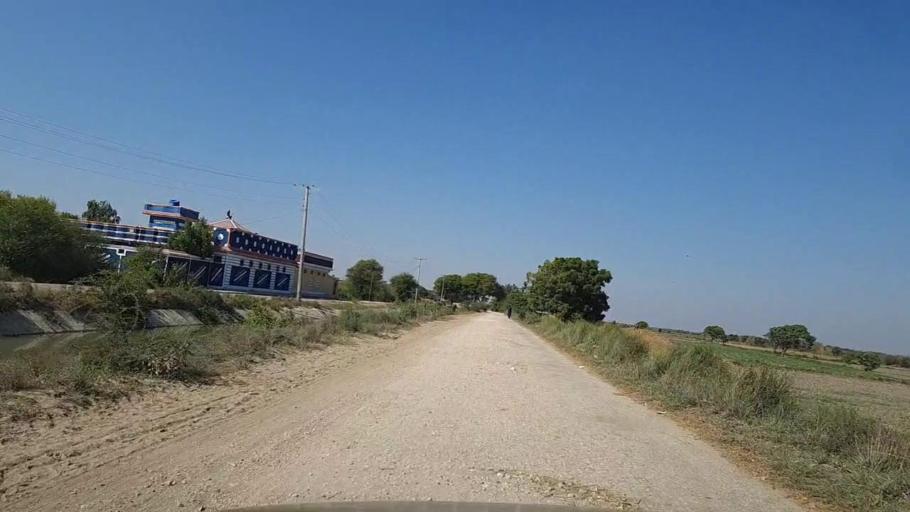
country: PK
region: Sindh
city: Mirpur Sakro
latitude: 24.6120
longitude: 67.7702
